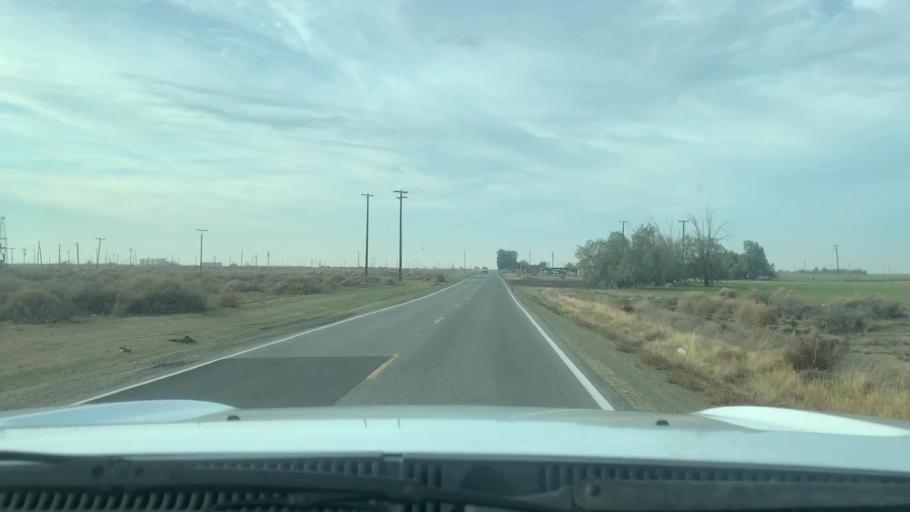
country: US
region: California
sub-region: Kern County
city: Lost Hills
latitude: 35.5346
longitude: -119.7689
